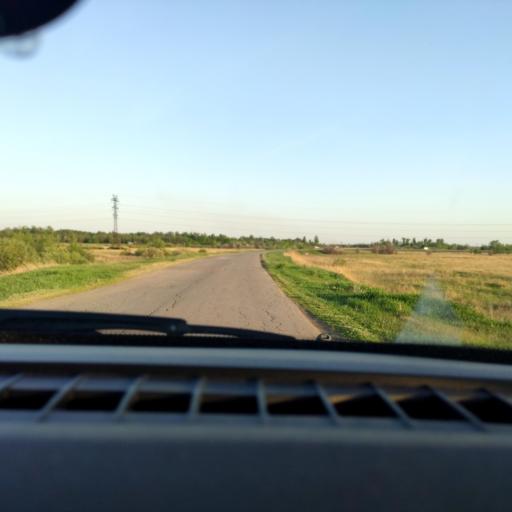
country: RU
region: Samara
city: Georgiyevka
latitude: 53.2677
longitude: 50.9606
